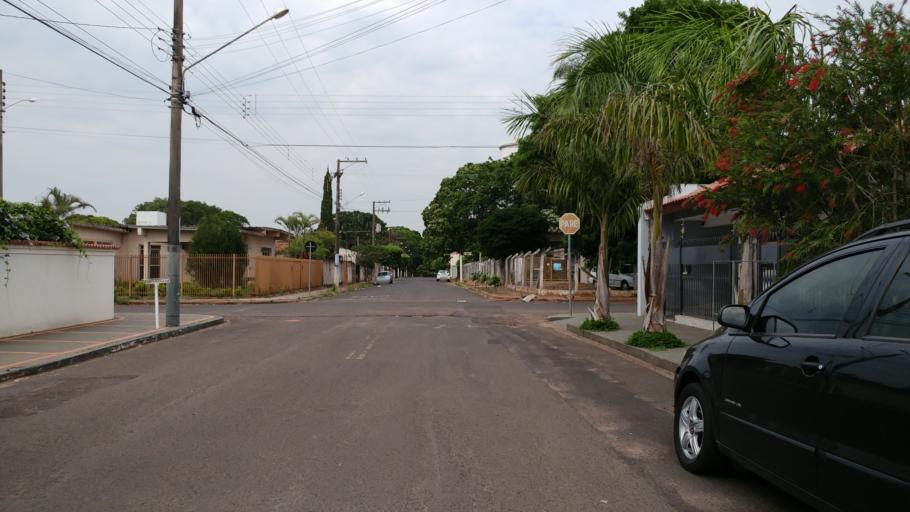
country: BR
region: Sao Paulo
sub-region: Paraguacu Paulista
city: Paraguacu Paulista
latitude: -22.4133
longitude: -50.5815
